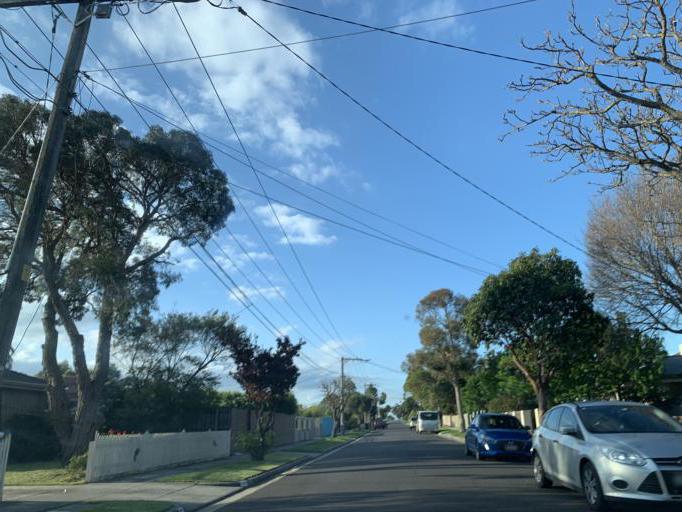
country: AU
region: Victoria
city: Heatherton
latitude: -37.9837
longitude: 145.0928
